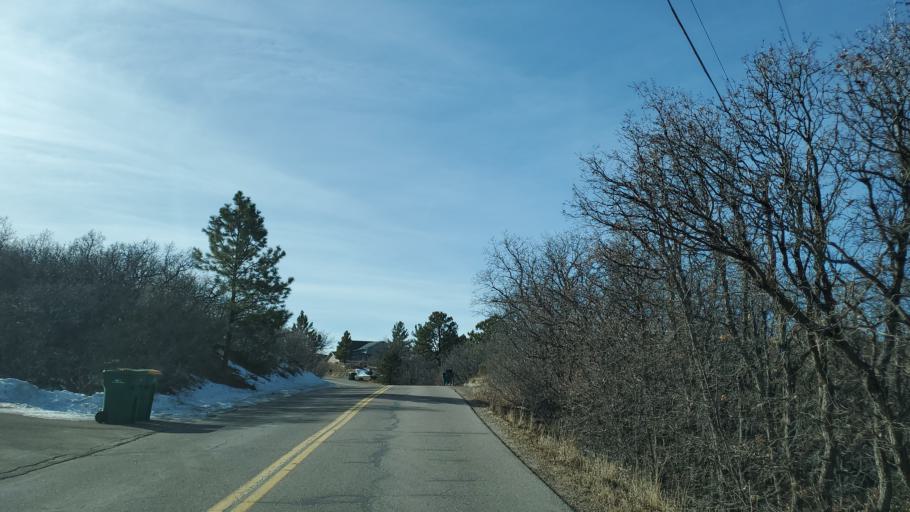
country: US
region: Colorado
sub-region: Douglas County
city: Castle Pines
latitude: 39.4433
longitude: -104.8721
